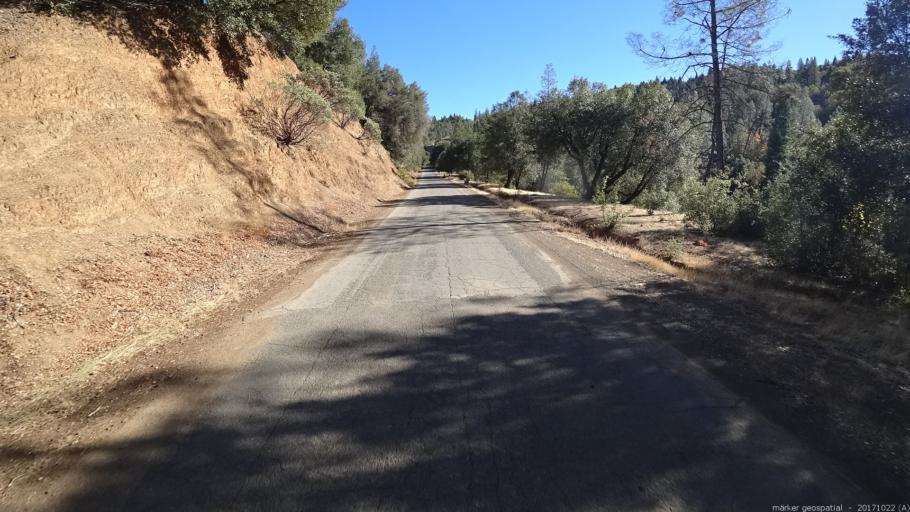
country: US
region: California
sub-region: Shasta County
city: Shasta Lake
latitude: 40.8744
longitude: -122.3634
